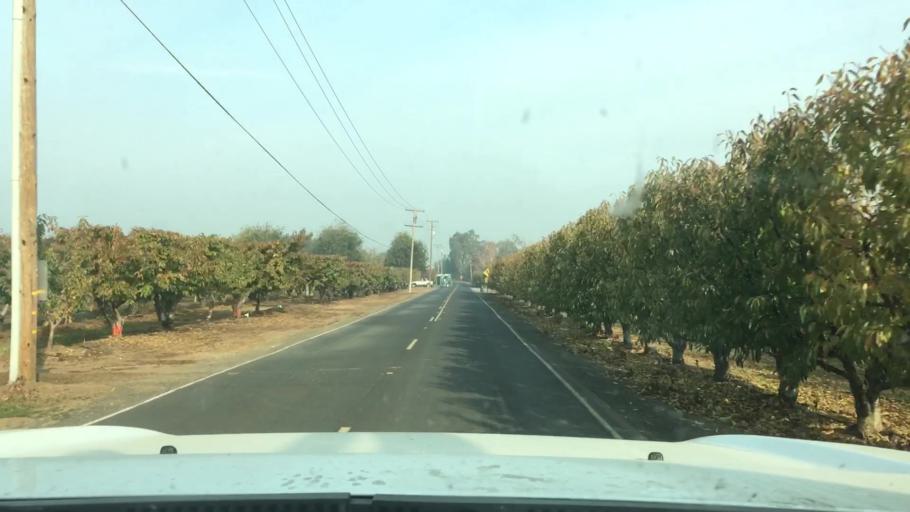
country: US
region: California
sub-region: San Joaquin County
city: Morada
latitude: 38.0422
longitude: -121.1985
